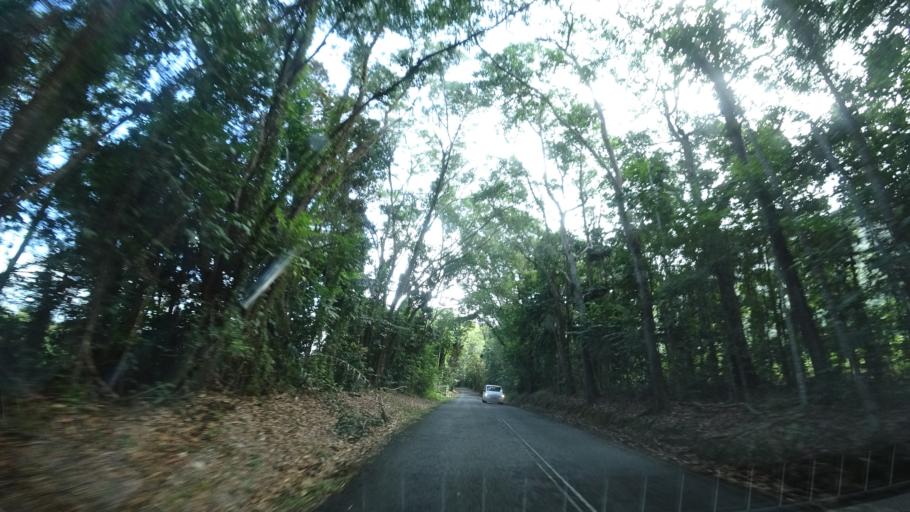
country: AU
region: Queensland
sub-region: Cairns
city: Port Douglas
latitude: -16.2547
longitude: 145.4177
